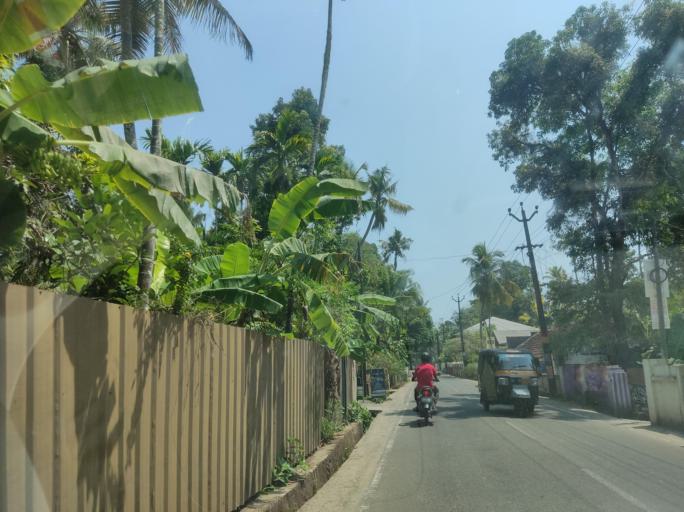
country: IN
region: Kerala
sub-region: Alappuzha
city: Kutiatodu
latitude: 9.7889
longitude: 76.3036
